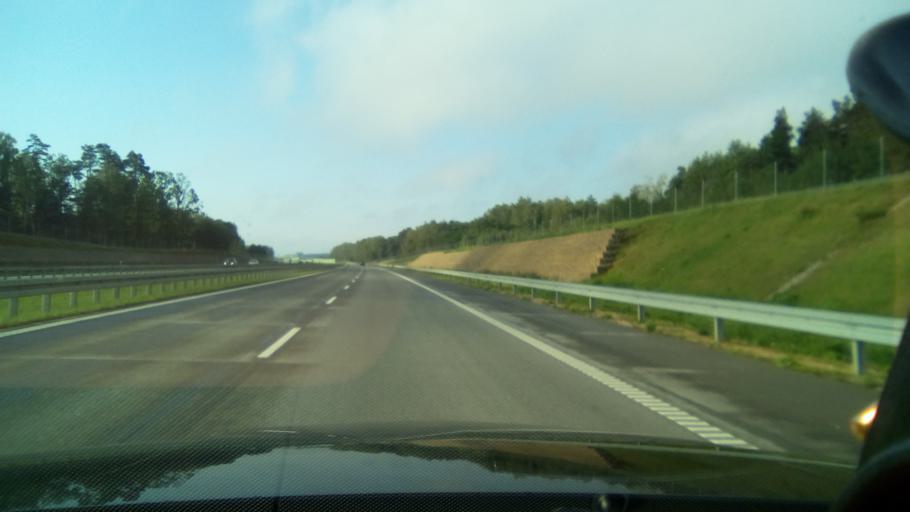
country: PL
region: Silesian Voivodeship
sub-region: Powiat czestochowski
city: Starcza
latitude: 50.6540
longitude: 19.0393
